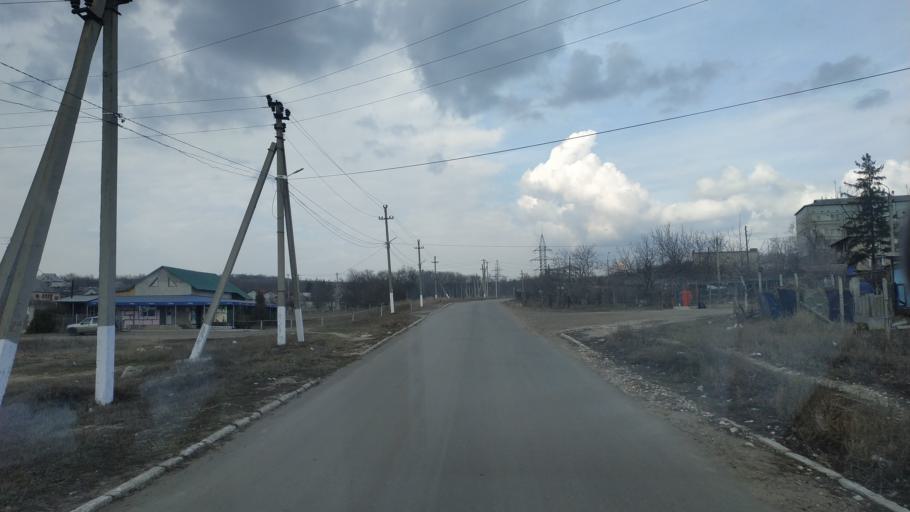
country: MD
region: Anenii Noi
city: Anenii Noi
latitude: 46.8913
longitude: 29.2819
